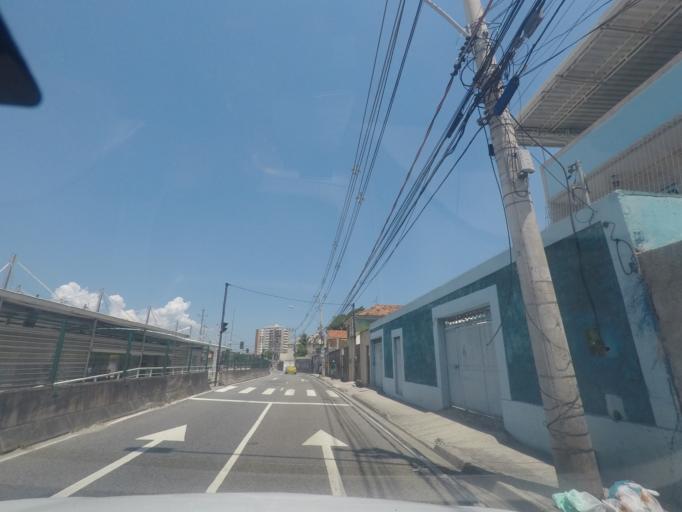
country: BR
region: Rio de Janeiro
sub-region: Duque De Caxias
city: Duque de Caxias
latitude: -22.8424
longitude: -43.2728
